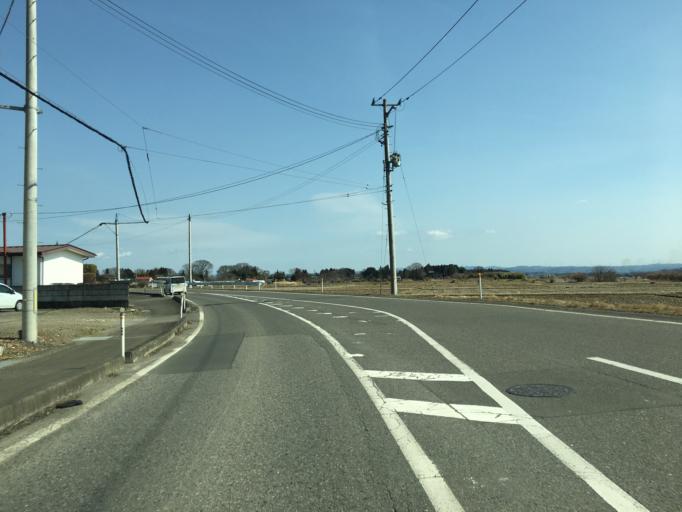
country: JP
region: Fukushima
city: Ishikawa
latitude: 37.1309
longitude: 140.3131
